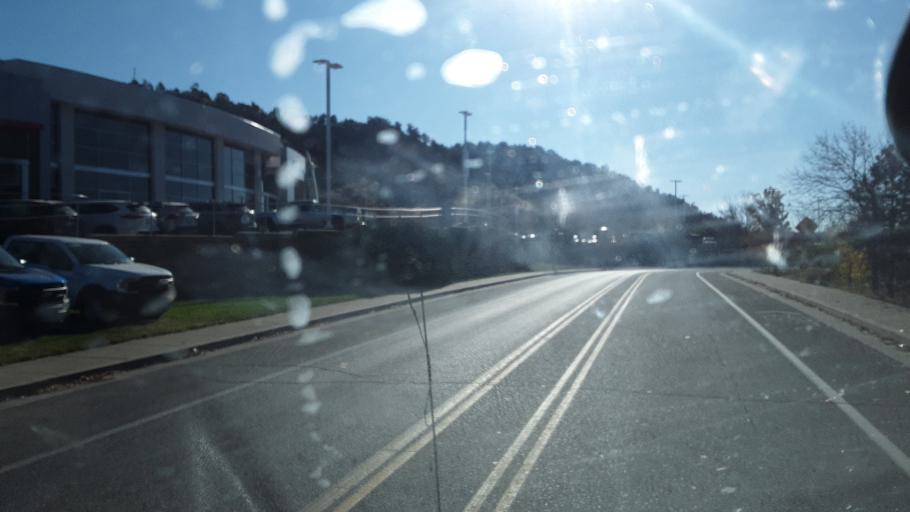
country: US
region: Colorado
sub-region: La Plata County
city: Durango
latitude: 37.2303
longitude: -107.8609
